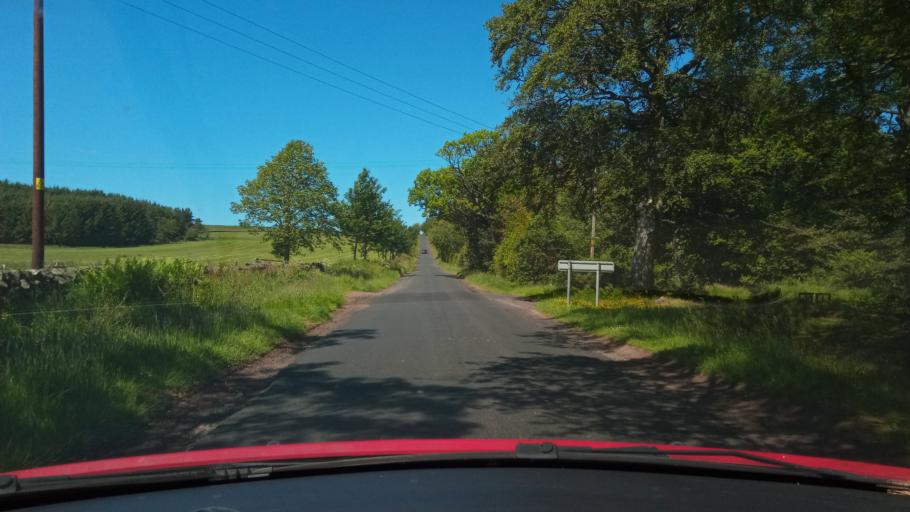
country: GB
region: Scotland
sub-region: The Scottish Borders
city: Duns
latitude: 55.8103
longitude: -2.4933
